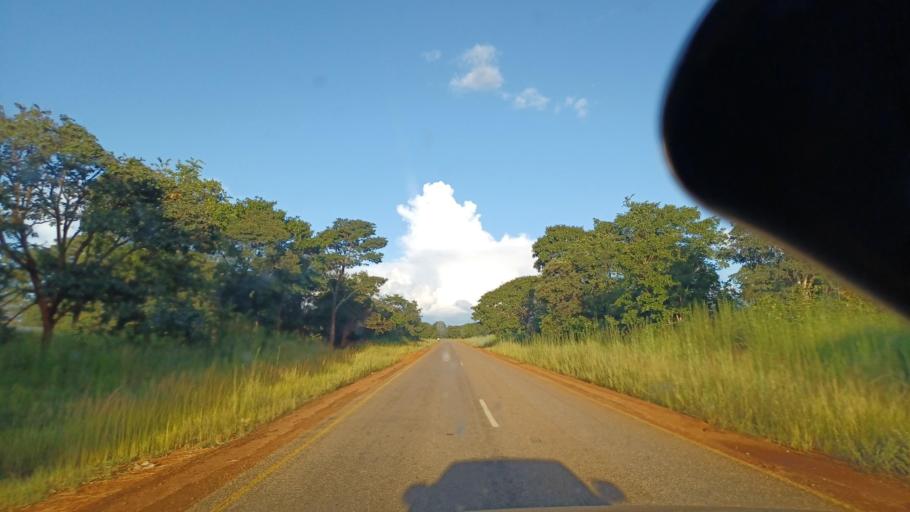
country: ZM
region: North-Western
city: Kalengwa
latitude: -13.1443
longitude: 25.0520
